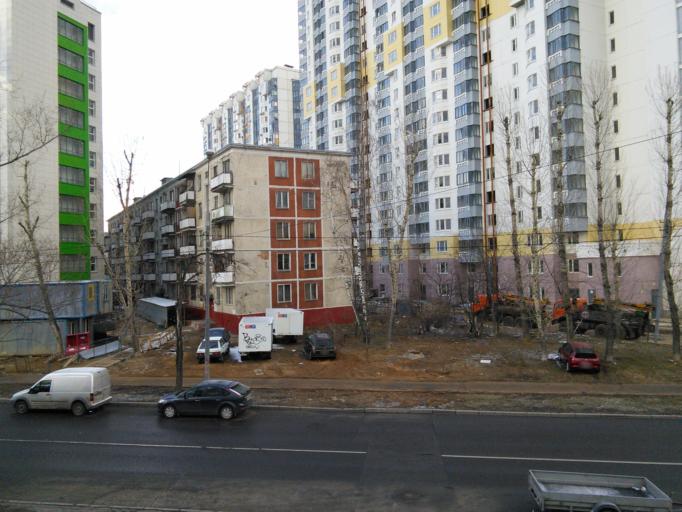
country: RU
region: Moscow
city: Davydkovo
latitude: 55.7300
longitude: 37.4641
